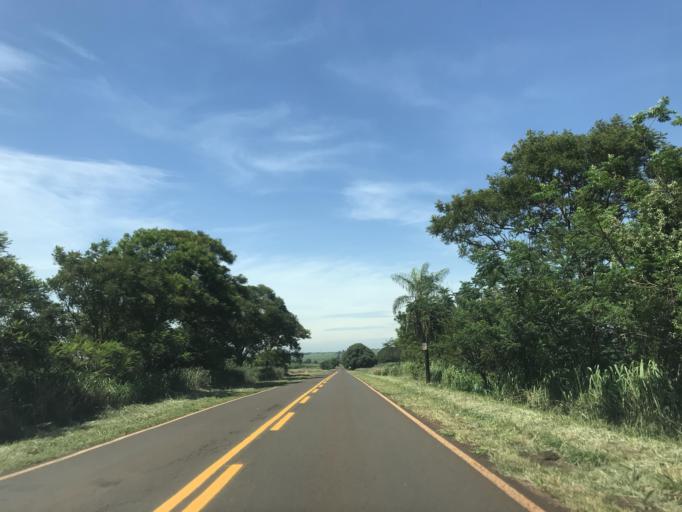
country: BR
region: Parana
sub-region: Terra Rica
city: Terra Rica
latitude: -22.8019
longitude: -52.6535
